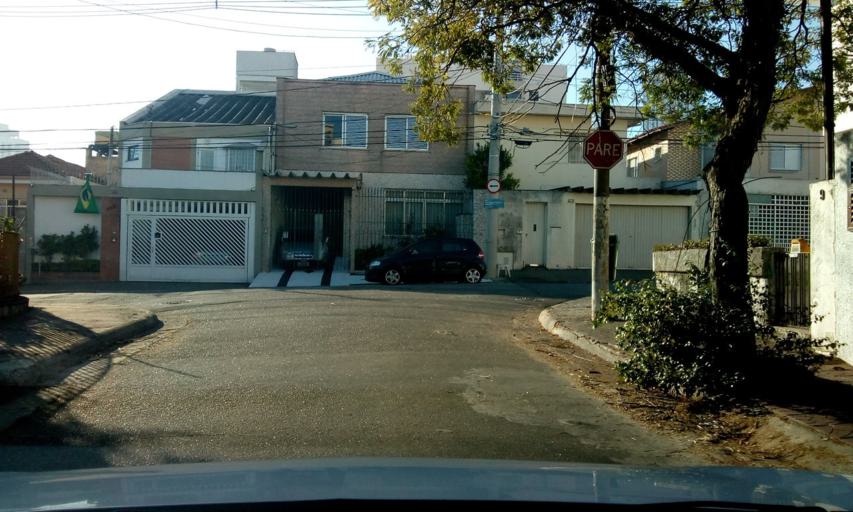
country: BR
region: Sao Paulo
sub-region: Sao Paulo
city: Sao Paulo
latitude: -23.5417
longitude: -46.6919
